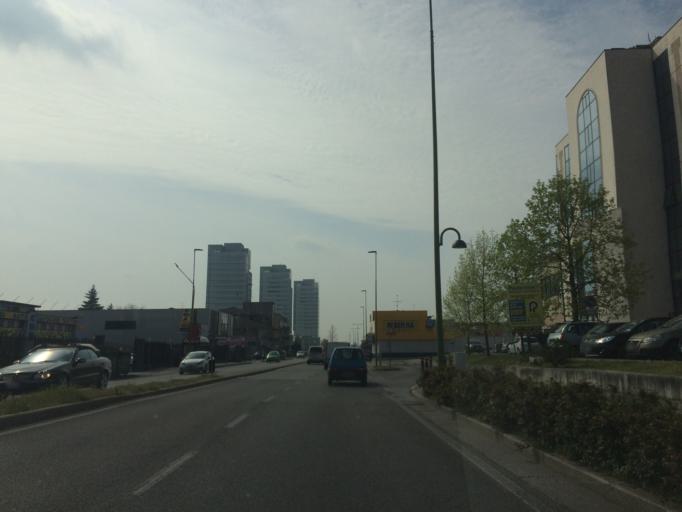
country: IT
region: Lombardy
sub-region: Provincia di Brescia
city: Brescia
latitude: 45.5262
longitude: 10.1981
